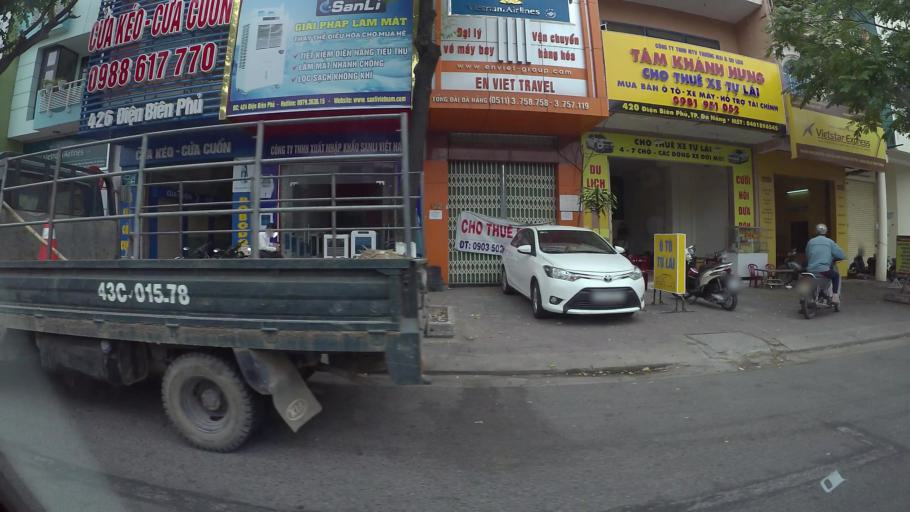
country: VN
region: Da Nang
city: Thanh Khe
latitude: 16.0660
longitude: 108.1890
